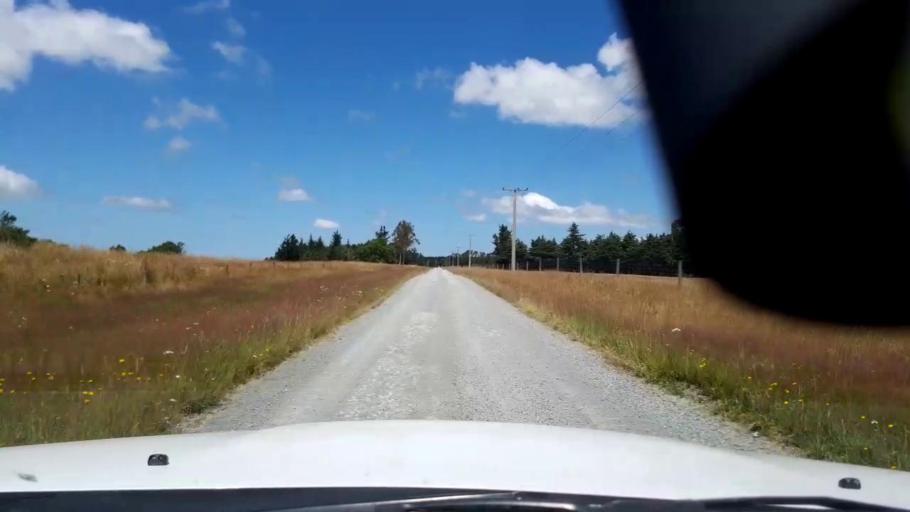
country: NZ
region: Canterbury
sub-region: Timaru District
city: Pleasant Point
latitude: -43.9856
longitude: 171.2890
